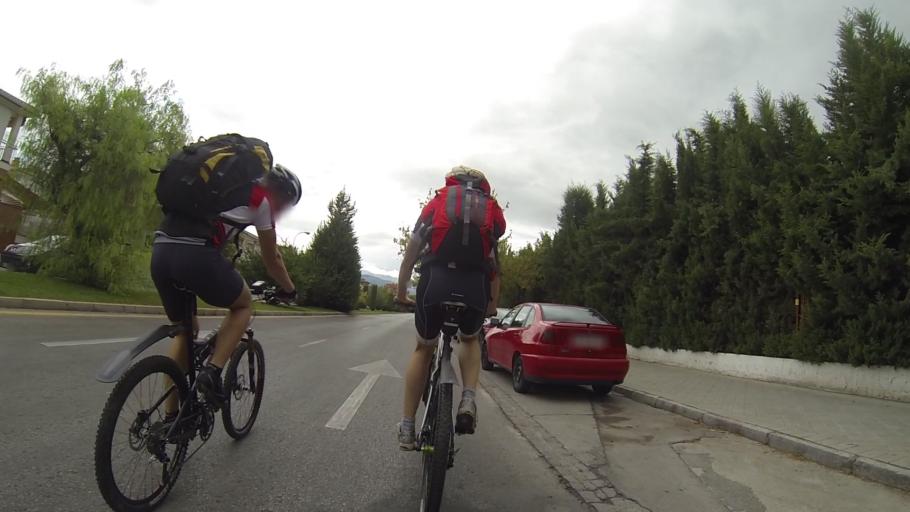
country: ES
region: Andalusia
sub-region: Provincia de Granada
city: Granada
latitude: 37.1935
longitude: -3.6172
